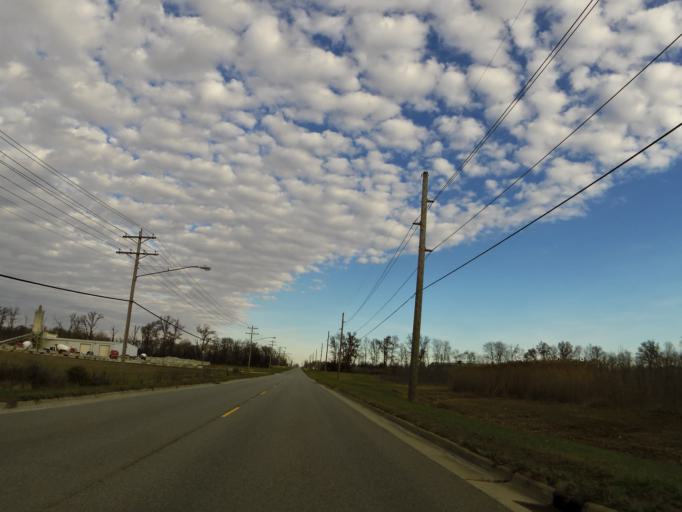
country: US
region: Illinois
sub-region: Jefferson County
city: Mount Vernon
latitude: 38.3195
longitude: -88.9700
